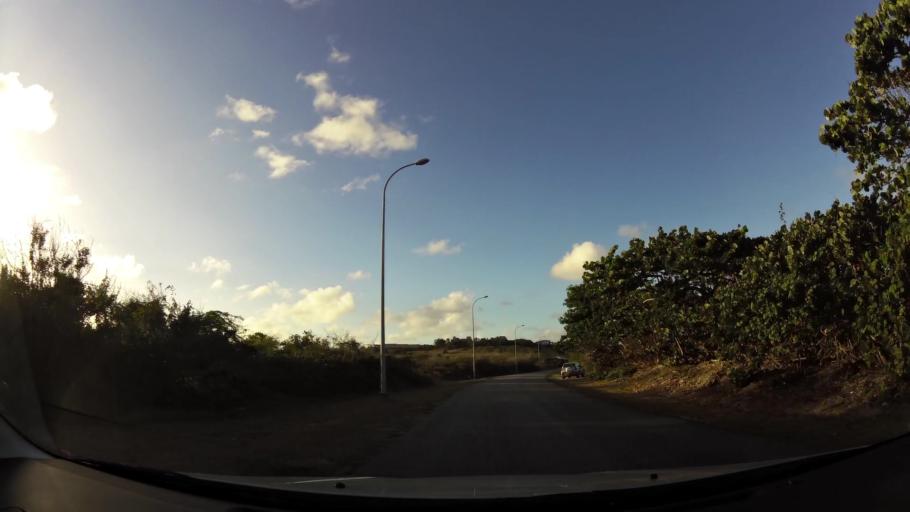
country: AG
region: Saint George
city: Piggotts
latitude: 17.1630
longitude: -61.7993
